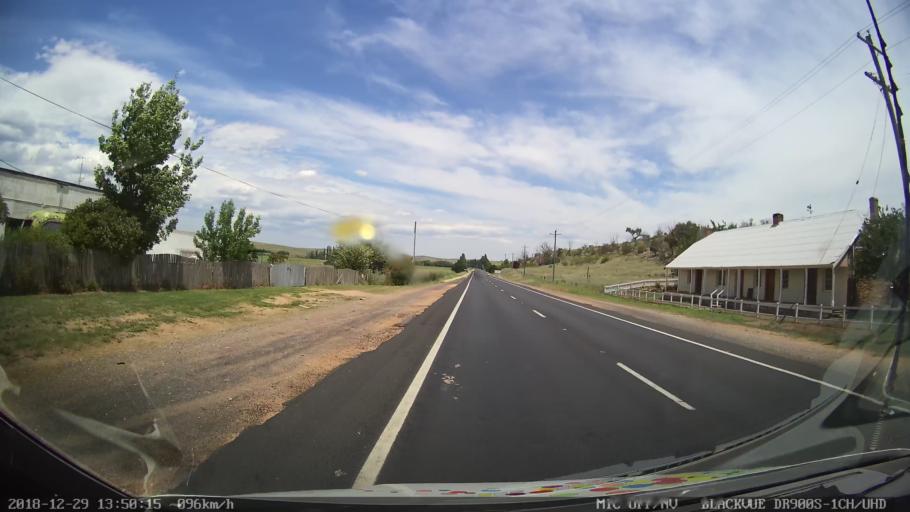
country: AU
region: New South Wales
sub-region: Cooma-Monaro
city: Cooma
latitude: -36.1654
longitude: 149.1533
